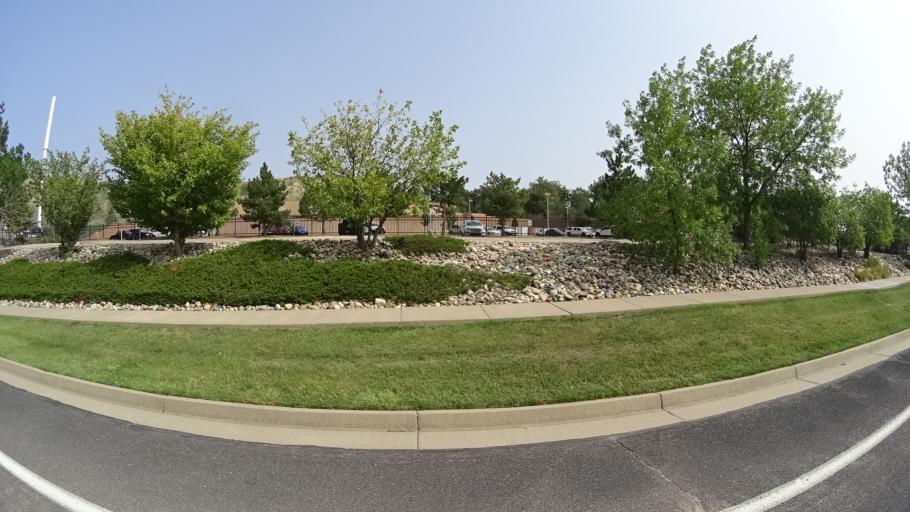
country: US
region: Colorado
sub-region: El Paso County
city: Colorado Springs
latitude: 38.8121
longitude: -104.8005
